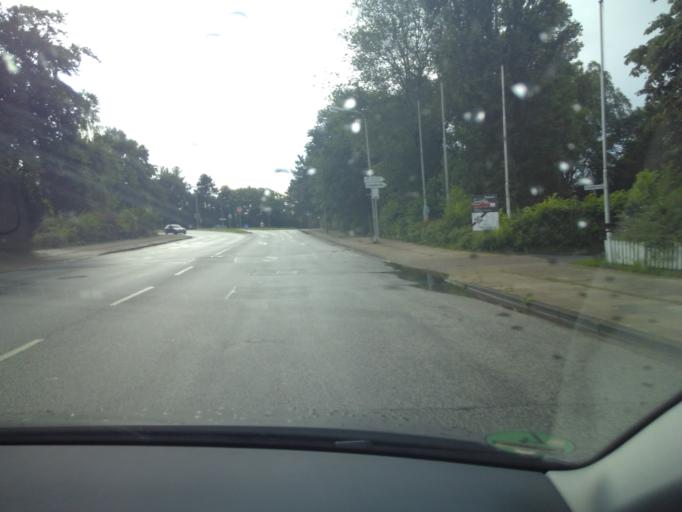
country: DE
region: Lower Saxony
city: Cuxhaven
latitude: 53.8741
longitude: 8.6809
